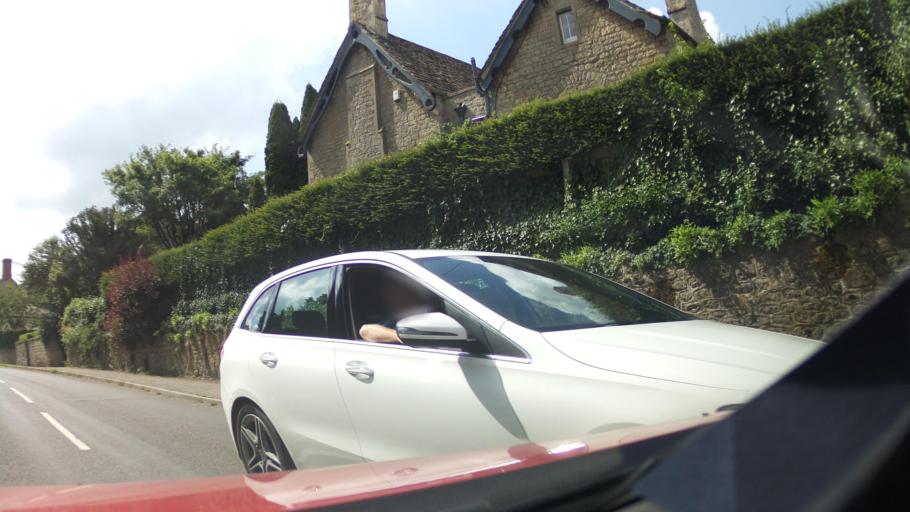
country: GB
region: England
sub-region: Wiltshire
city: Purton
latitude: 51.5872
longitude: -1.8662
